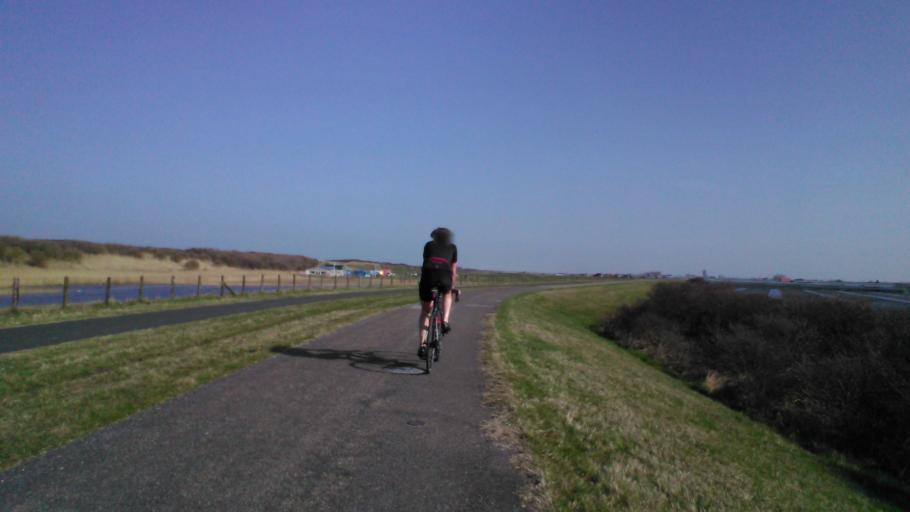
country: NL
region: South Holland
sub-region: Gemeente Westland
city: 's-Gravenzande
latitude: 52.0071
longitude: 4.1420
